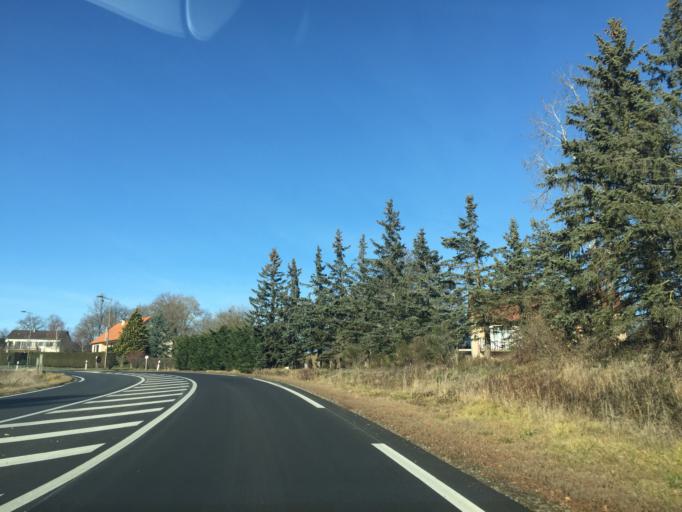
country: FR
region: Auvergne
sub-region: Departement du Puy-de-Dome
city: Saint-Ours
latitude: 45.8339
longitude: 2.8318
